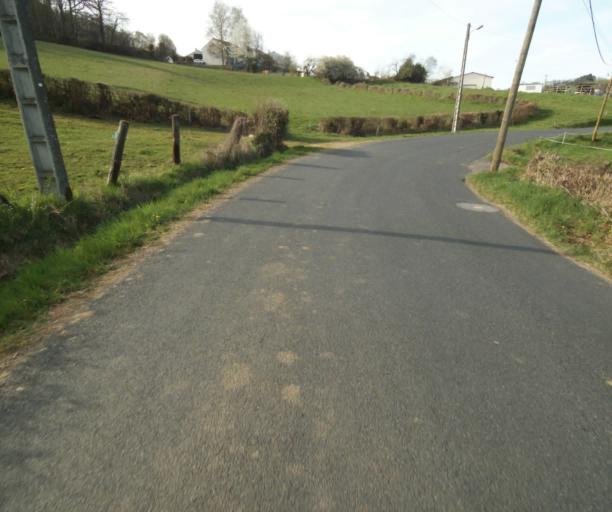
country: FR
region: Limousin
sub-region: Departement de la Correze
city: Tulle
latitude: 45.2860
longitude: 1.7602
